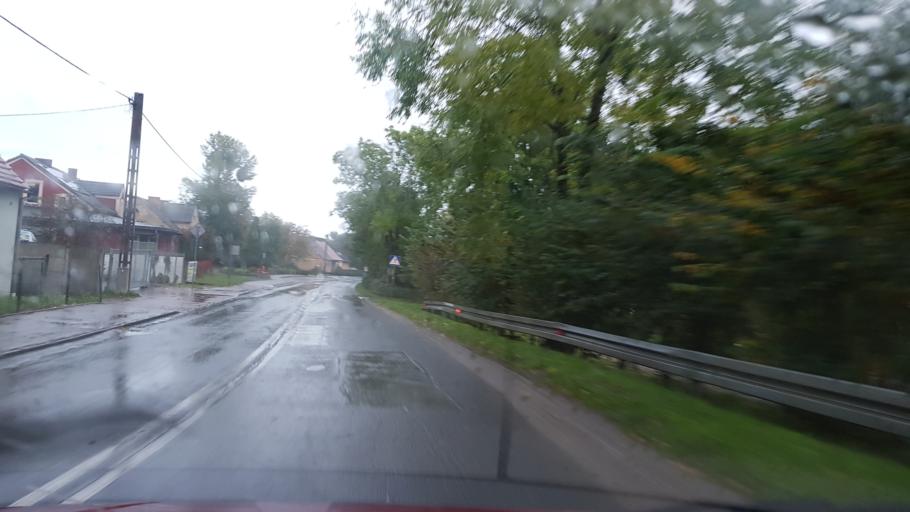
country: PL
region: Greater Poland Voivodeship
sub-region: Powiat pilski
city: Szydlowo
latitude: 53.1621
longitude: 16.6122
